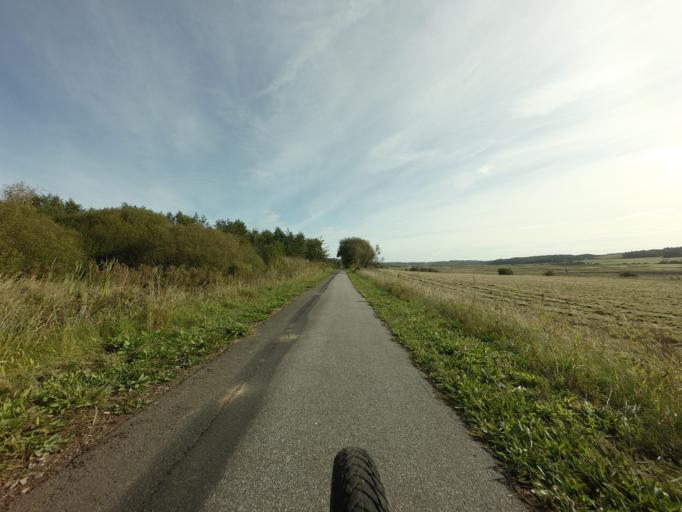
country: DK
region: Central Jutland
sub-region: Viborg Kommune
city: Viborg
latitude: 56.4386
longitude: 9.5067
